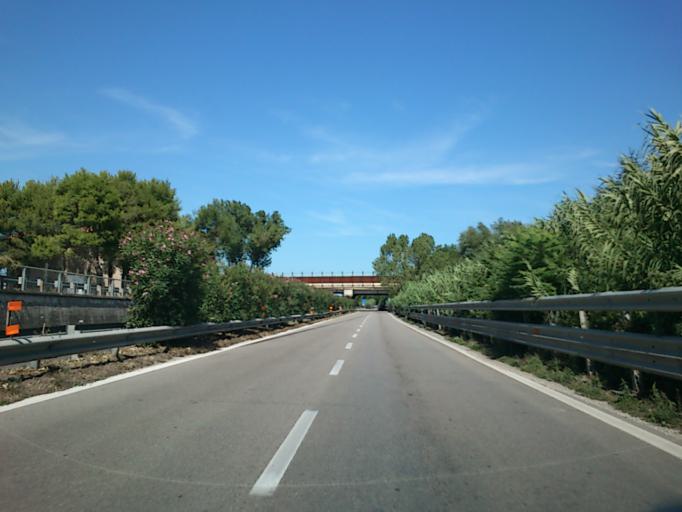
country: IT
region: The Marches
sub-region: Provincia di Pesaro e Urbino
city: Rosciano
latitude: 43.8124
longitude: 13.0181
